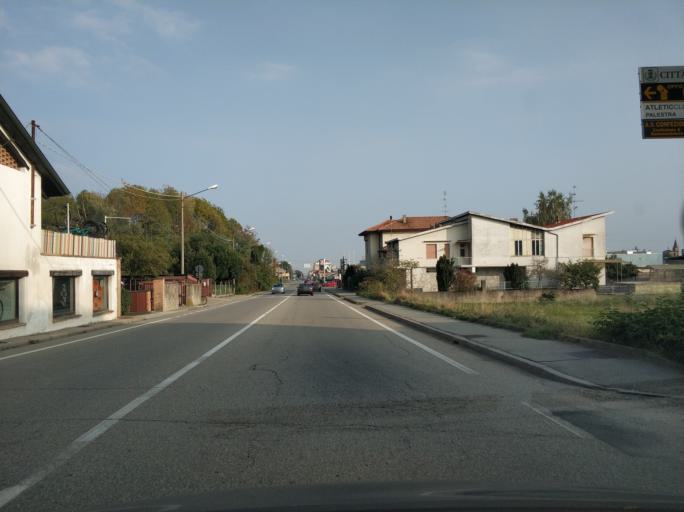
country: IT
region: Piedmont
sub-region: Provincia di Biella
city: Ronco Biellese
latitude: 45.5666
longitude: 8.0868
